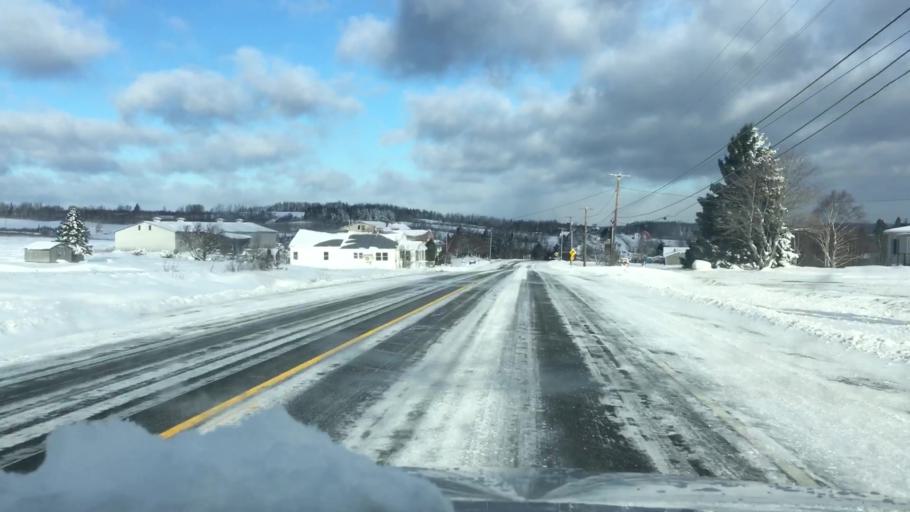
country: US
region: Maine
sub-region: Aroostook County
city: Caribou
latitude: 46.9525
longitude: -68.0254
